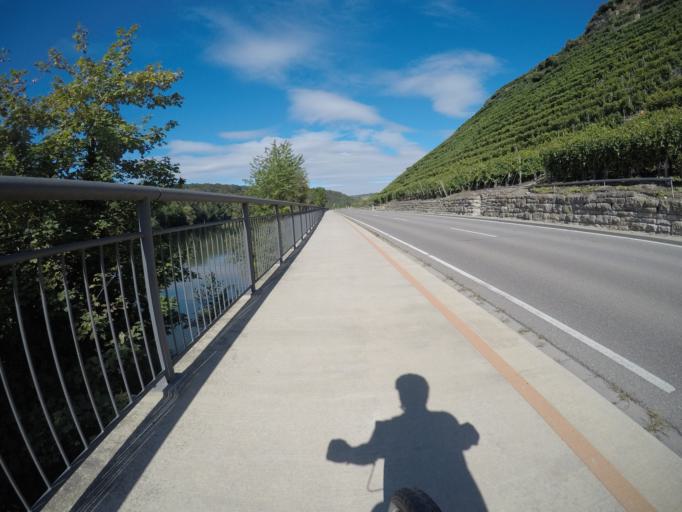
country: DE
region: Baden-Wuerttemberg
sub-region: Regierungsbezirk Stuttgart
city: Mundelsheim
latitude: 48.9848
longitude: 9.2124
